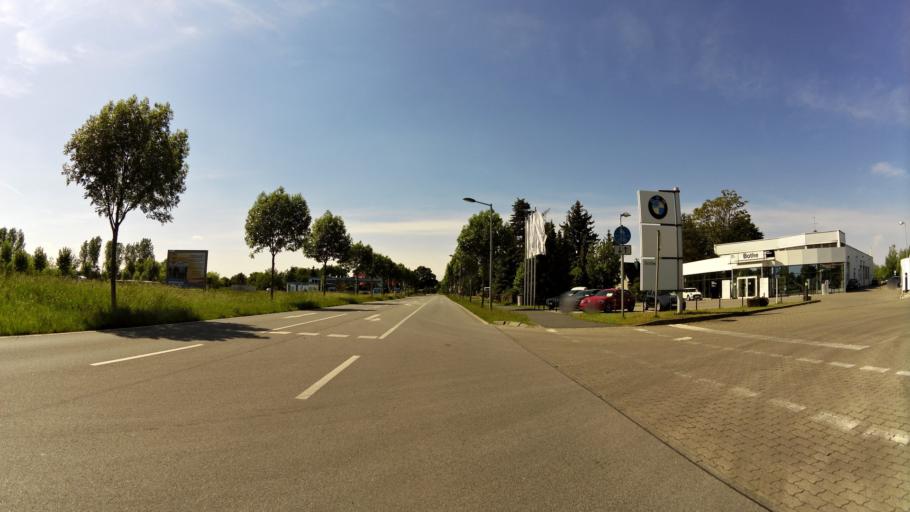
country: DE
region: Brandenburg
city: Frankfurt (Oder)
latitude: 52.3648
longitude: 14.5244
